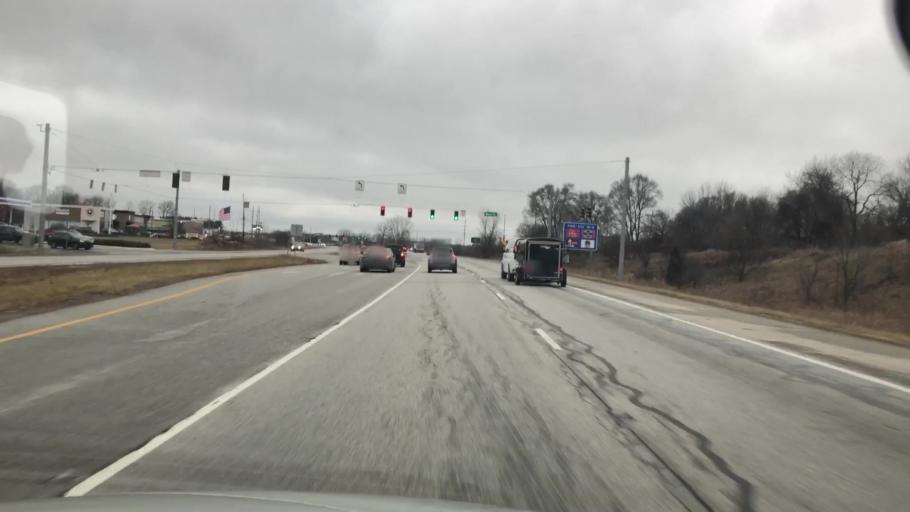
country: US
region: Indiana
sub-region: Kosciusko County
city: Warsaw
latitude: 41.2614
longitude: -85.8373
